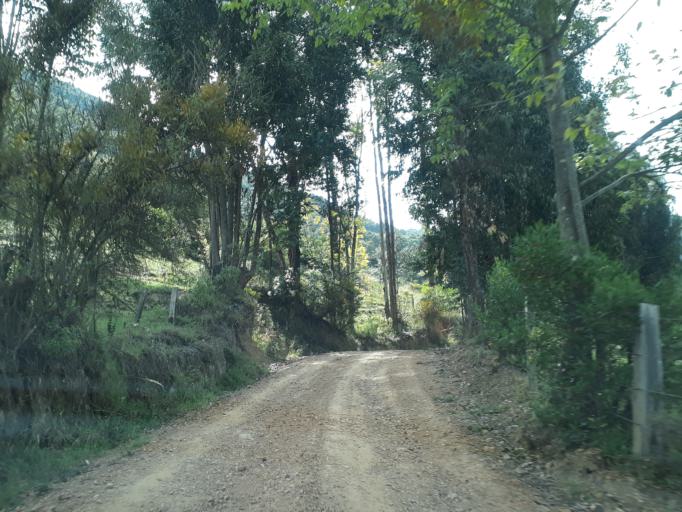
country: CO
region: Boyaca
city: Santa Rosa de Viterbo
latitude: 5.8544
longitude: -72.9674
